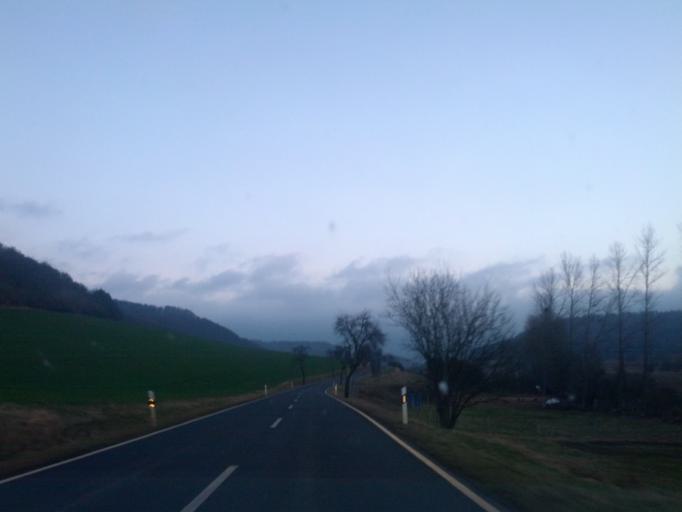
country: DE
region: Thuringia
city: Treffurt
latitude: 51.0982
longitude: 10.2169
